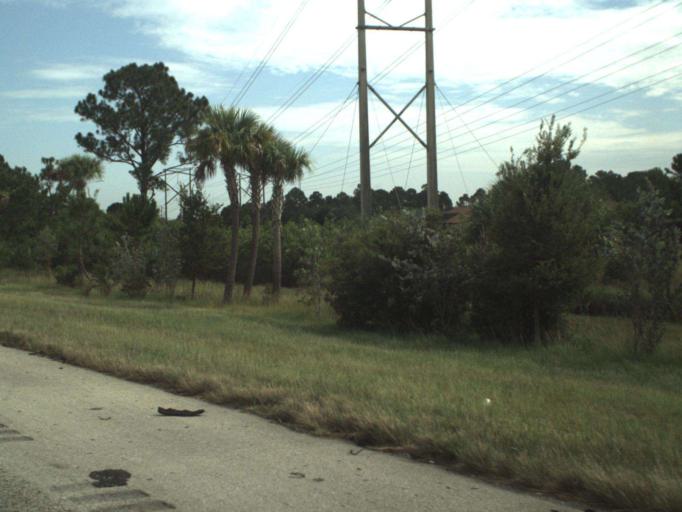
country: US
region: Florida
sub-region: Saint Lucie County
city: Port Saint Lucie
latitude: 27.2498
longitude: -80.4158
